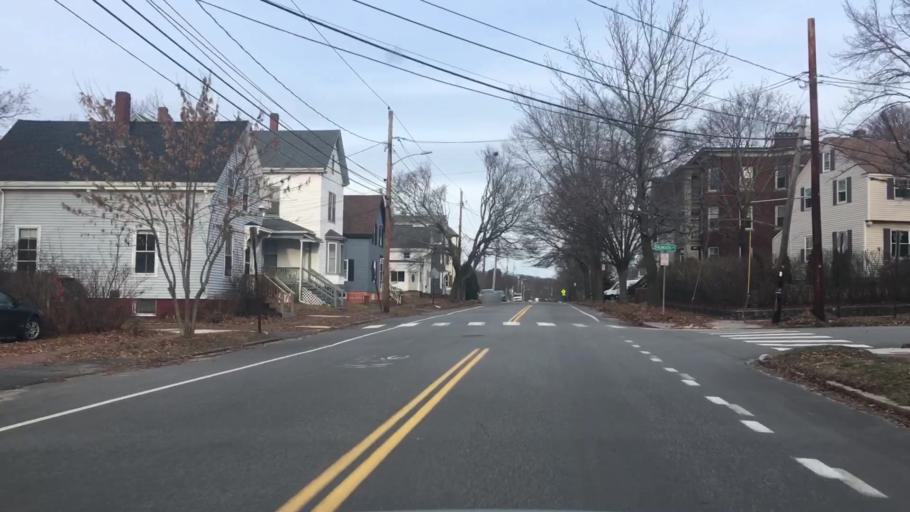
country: US
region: Maine
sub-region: Cumberland County
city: Portland
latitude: 43.6591
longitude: -70.2826
